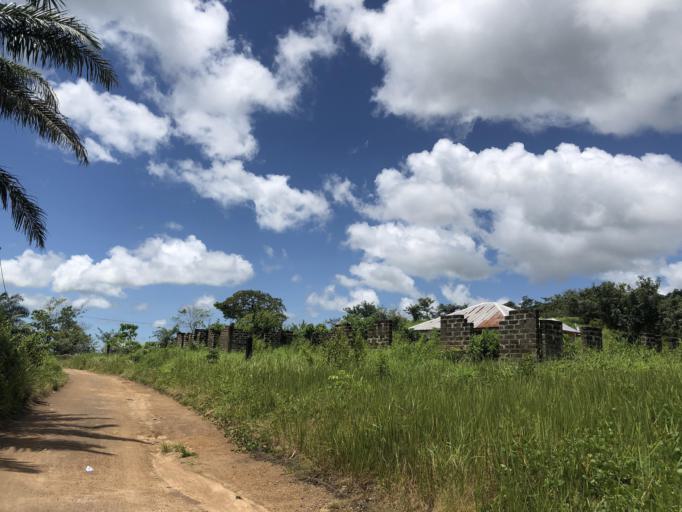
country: SL
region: Northern Province
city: Makeni
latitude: 8.8491
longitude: -12.0603
